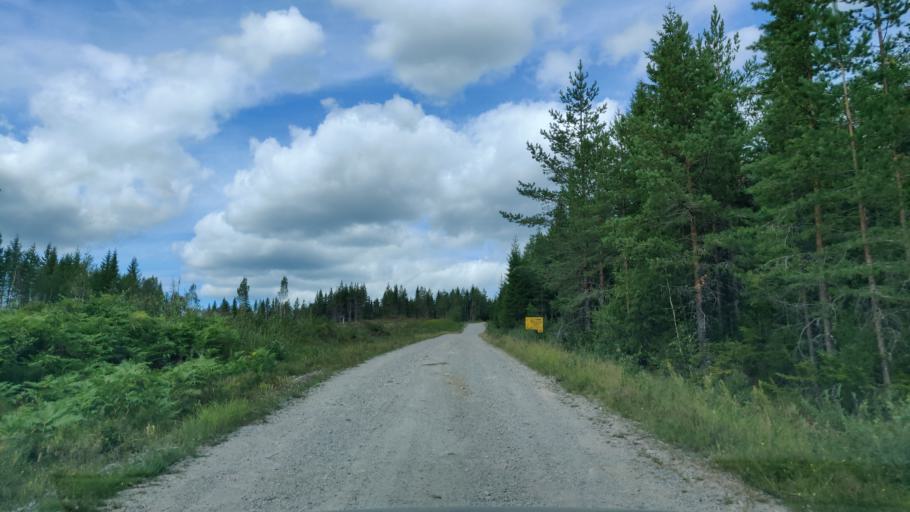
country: SE
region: Vaermland
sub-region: Hagfors Kommun
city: Hagfors
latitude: 60.0185
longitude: 13.7305
